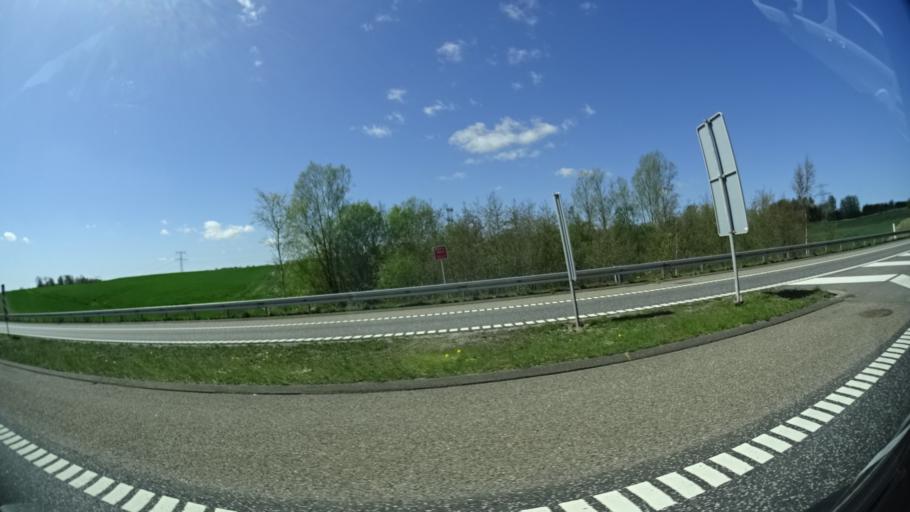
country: DK
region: Central Jutland
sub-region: Arhus Kommune
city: Trige
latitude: 56.2290
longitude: 10.1231
